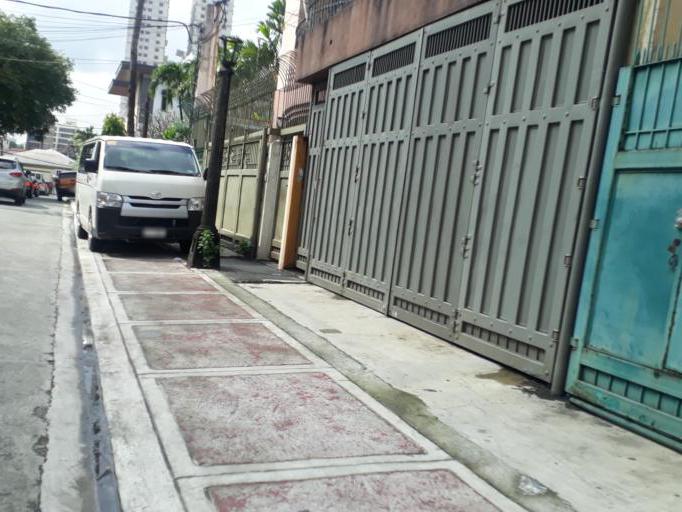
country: PH
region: Metro Manila
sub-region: San Juan
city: San Juan
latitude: 14.6142
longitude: 121.0286
